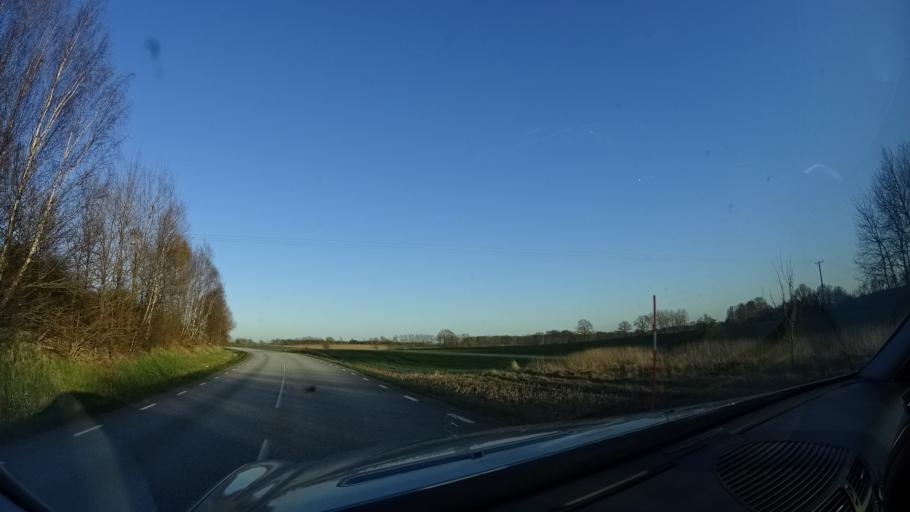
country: SE
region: Skane
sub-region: Klippans Kommun
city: Ljungbyhed
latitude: 55.9666
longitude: 13.2168
